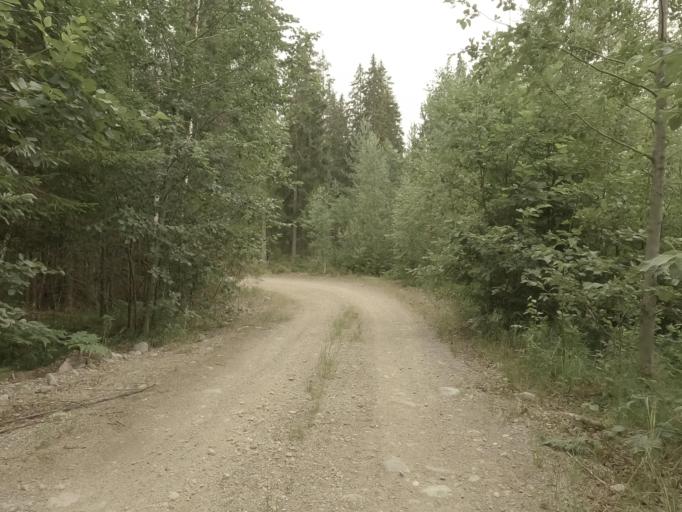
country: RU
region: Leningrad
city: Kamennogorsk
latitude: 61.0410
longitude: 29.1860
